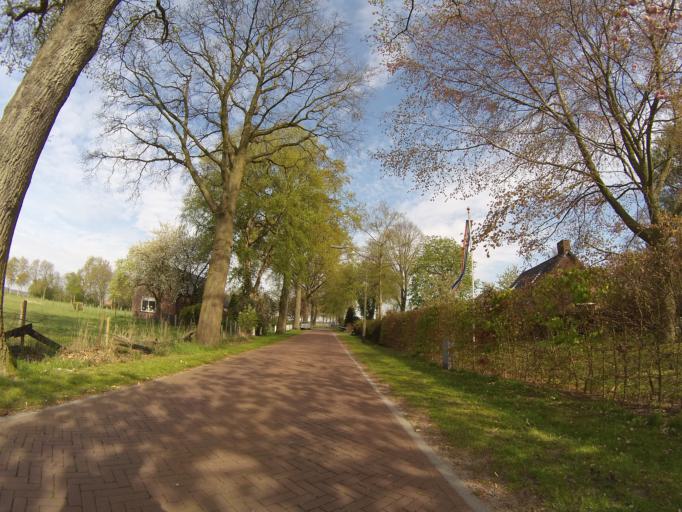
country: NL
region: Drenthe
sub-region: Gemeente Coevorden
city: Sleen
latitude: 52.7789
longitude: 6.7971
